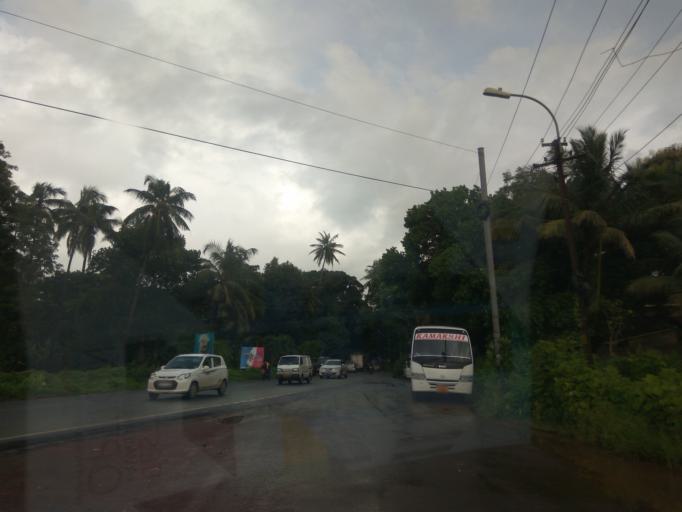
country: IN
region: Goa
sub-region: North Goa
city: Goa Velha
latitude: 15.4413
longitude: 73.8686
